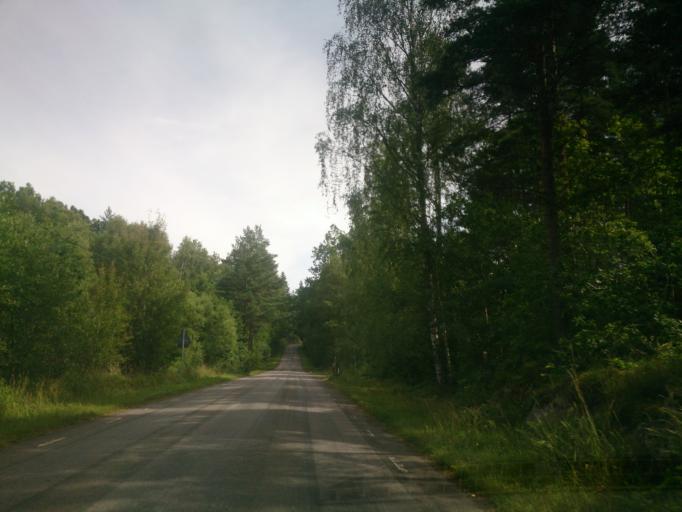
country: SE
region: OEstergoetland
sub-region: Soderkopings Kommun
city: Soederkoeping
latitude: 58.2837
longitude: 16.2310
